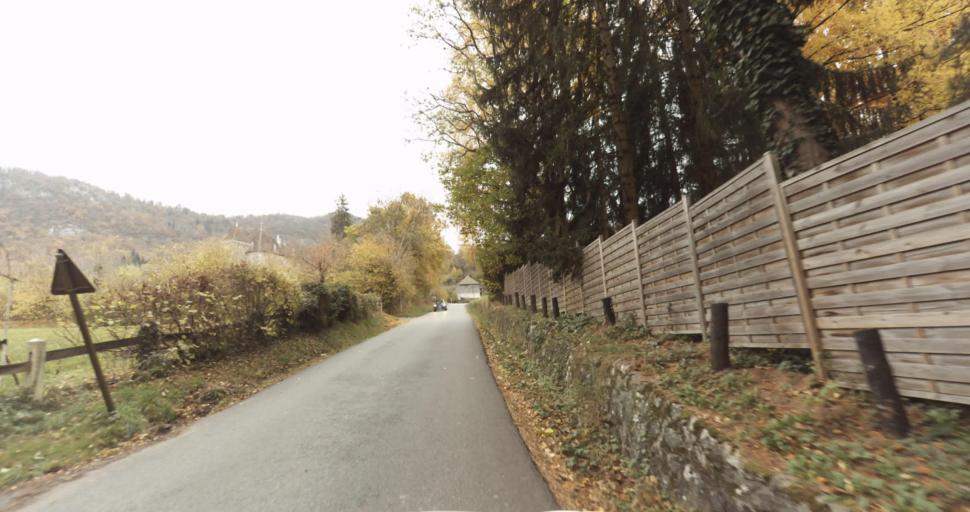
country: FR
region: Rhone-Alpes
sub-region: Departement de la Haute-Savoie
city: Talloires
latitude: 45.8252
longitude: 6.1966
